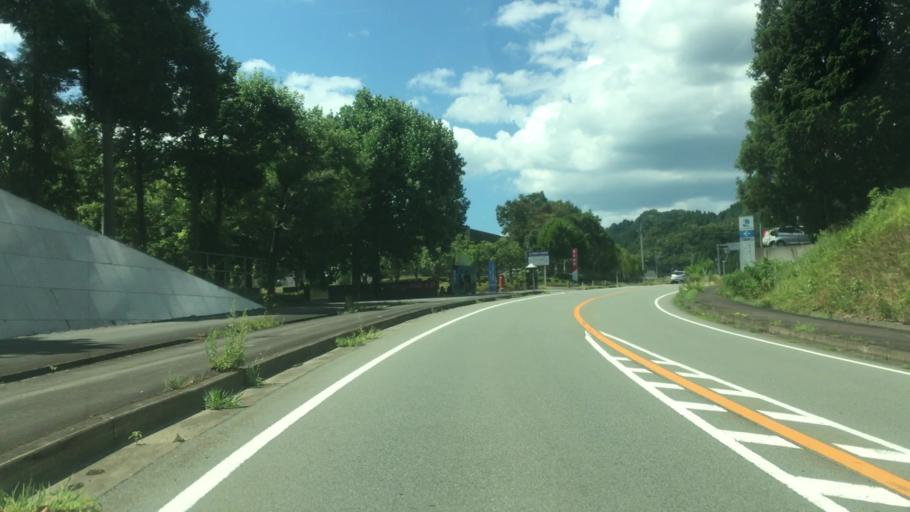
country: JP
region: Hyogo
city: Toyooka
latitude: 35.4618
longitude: 134.7334
